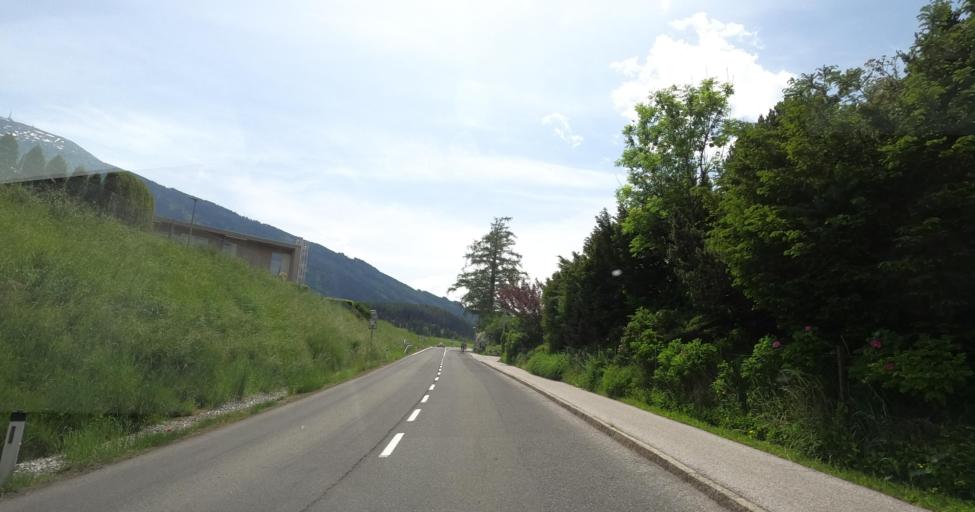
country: AT
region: Tyrol
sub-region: Politischer Bezirk Innsbruck Land
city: Sistrans
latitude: 47.2366
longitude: 11.4329
